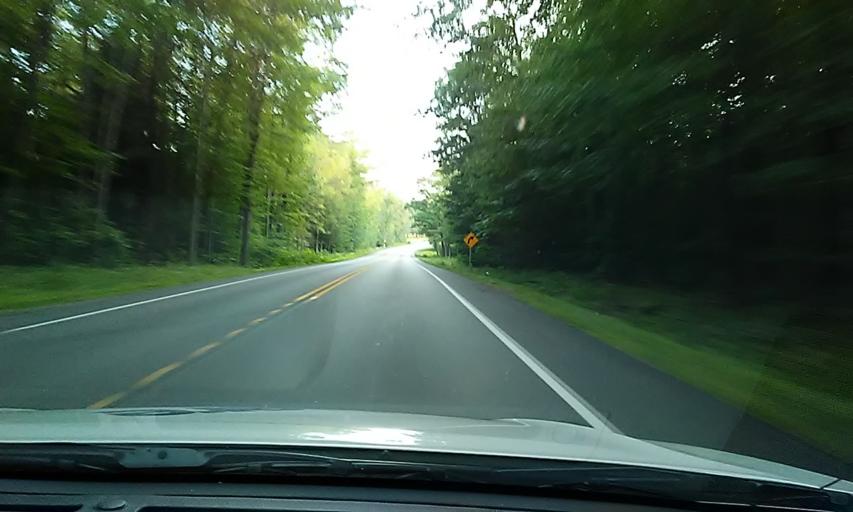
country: US
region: Pennsylvania
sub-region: Forest County
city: Marienville
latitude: 41.5088
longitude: -79.0733
